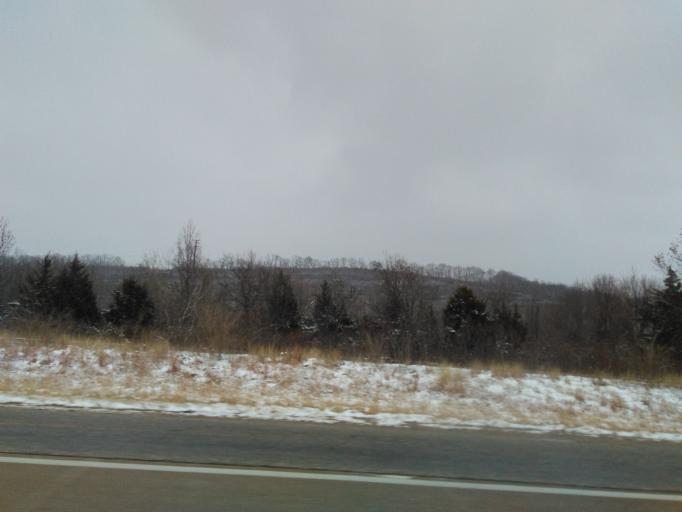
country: US
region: Illinois
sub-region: Saint Clair County
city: Dupo
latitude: 38.5169
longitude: -90.2001
